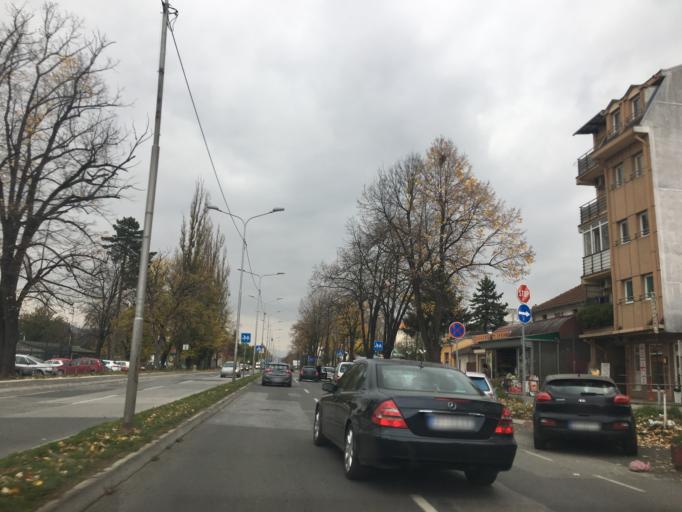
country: RS
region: Central Serbia
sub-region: Raski Okrug
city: Kraljevo
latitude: 43.7254
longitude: 20.6986
